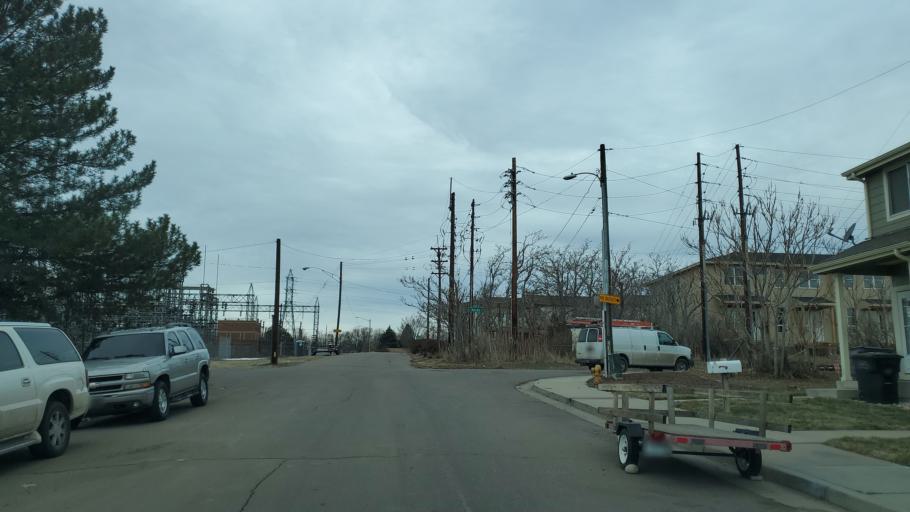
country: US
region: Colorado
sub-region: Denver County
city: Denver
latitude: 39.6949
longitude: -105.0035
